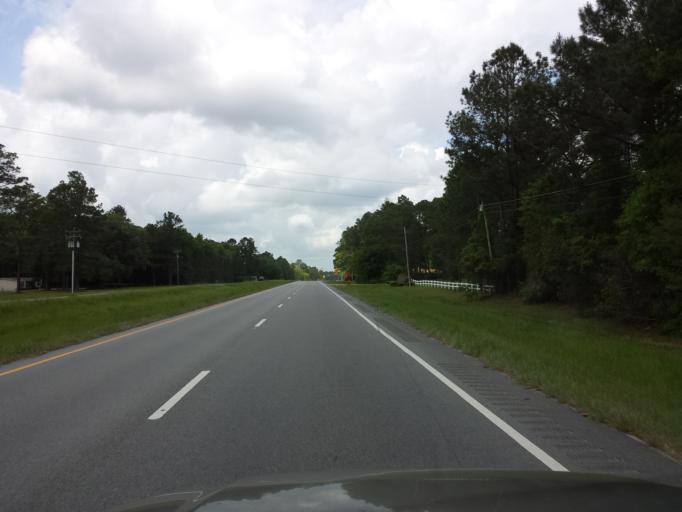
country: US
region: Georgia
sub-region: Lowndes County
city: Valdosta
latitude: 30.7126
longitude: -83.2141
